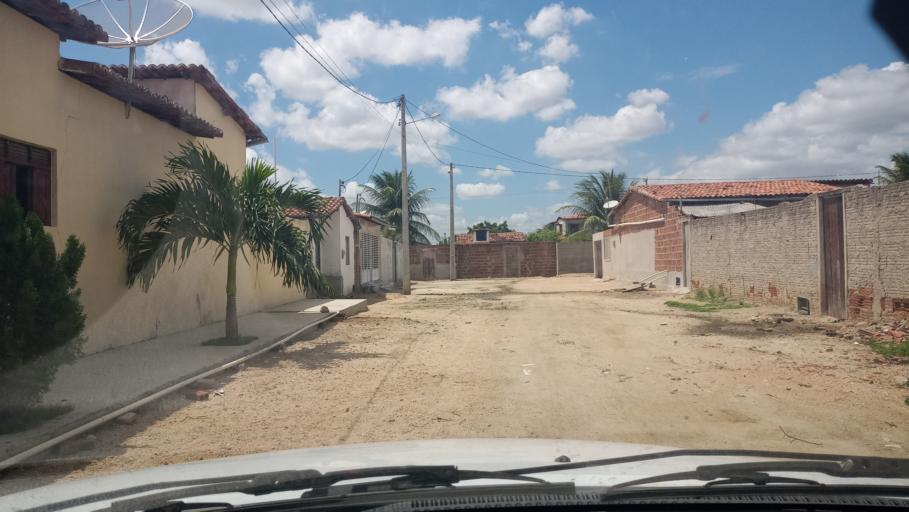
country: BR
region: Rio Grande do Norte
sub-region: Nova Cruz
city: Nova Cruz
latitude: -6.4577
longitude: -35.5795
